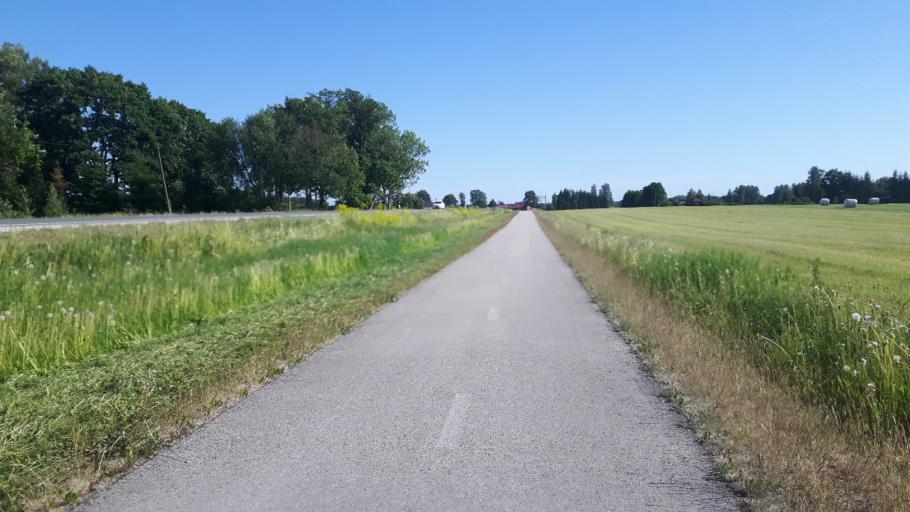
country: EE
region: Raplamaa
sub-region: Kehtna vald
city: Kehtna
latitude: 58.9464
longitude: 24.8767
